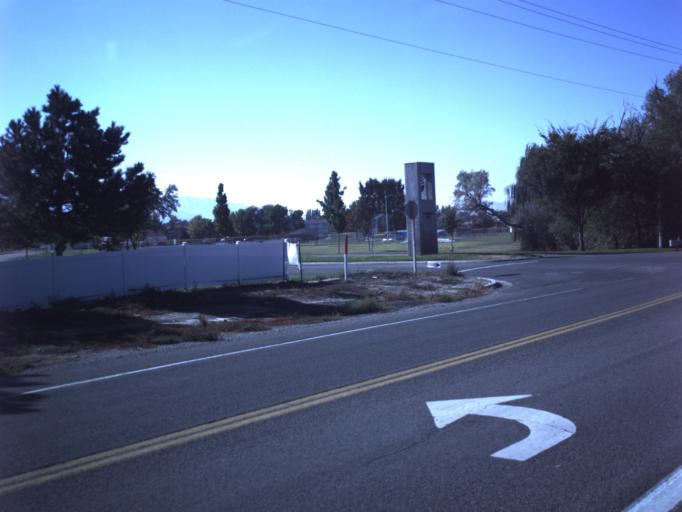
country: US
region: Utah
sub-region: Tooele County
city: Stansbury park
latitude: 40.6511
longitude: -112.2960
